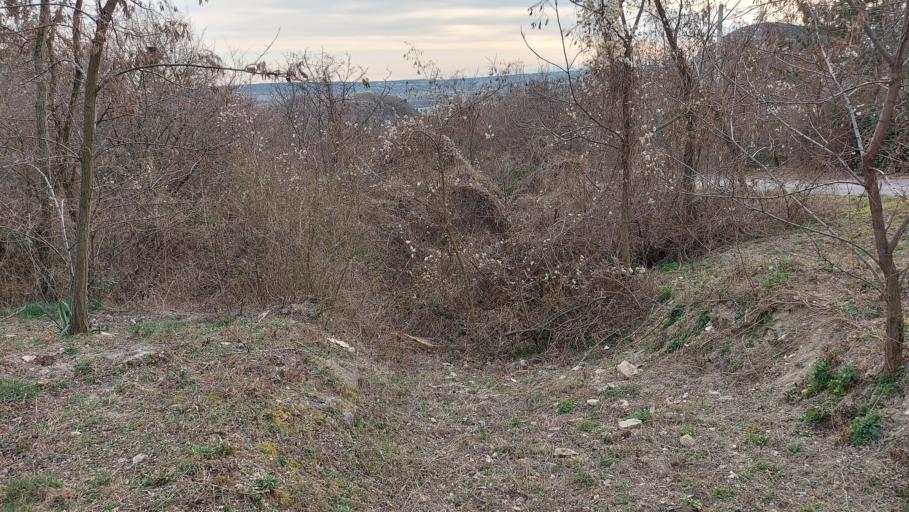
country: HU
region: Pest
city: Budaors
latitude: 47.4719
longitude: 18.9633
